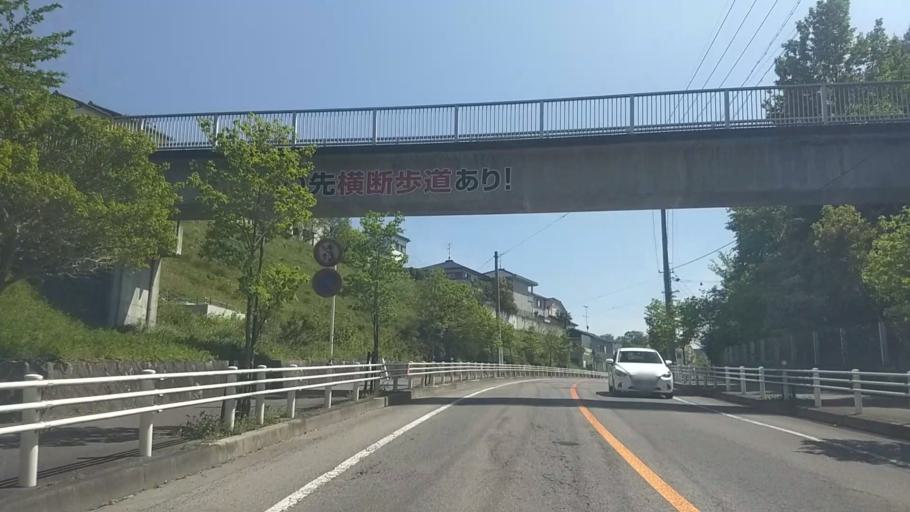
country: JP
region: Aichi
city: Okazaki
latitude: 34.9796
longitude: 137.2001
